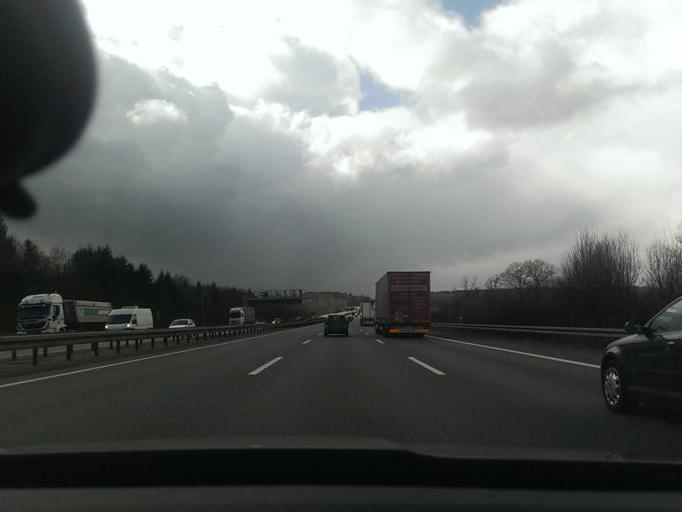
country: DE
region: Lower Saxony
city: Lehre
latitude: 52.3081
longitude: 10.7128
